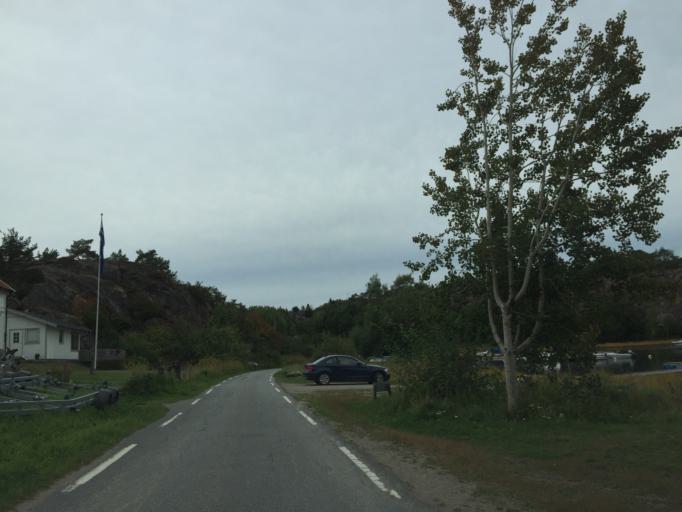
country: NO
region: Ostfold
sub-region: Hvaler
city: Skjaerhalden
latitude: 59.0372
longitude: 11.0523
